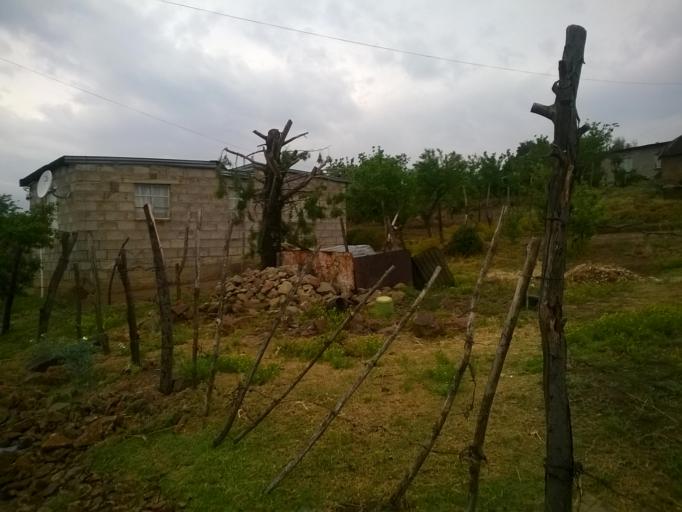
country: LS
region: Berea
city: Teyateyaneng
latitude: -29.1362
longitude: 27.7369
